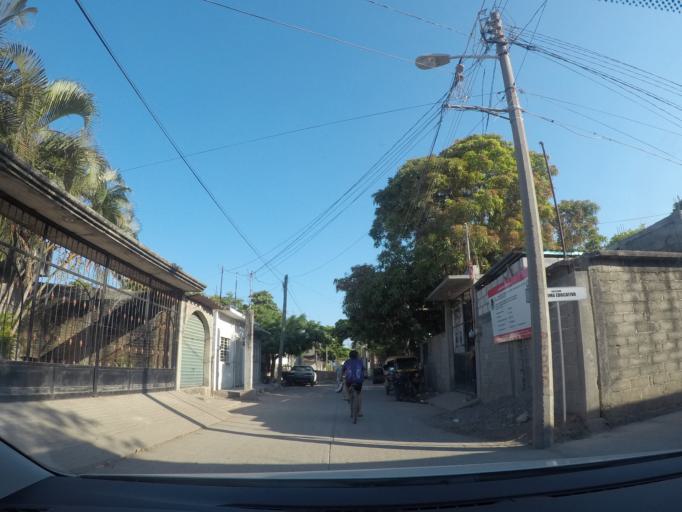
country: MX
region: Oaxaca
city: Juchitan de Zaragoza
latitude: 16.4214
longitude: -95.0269
